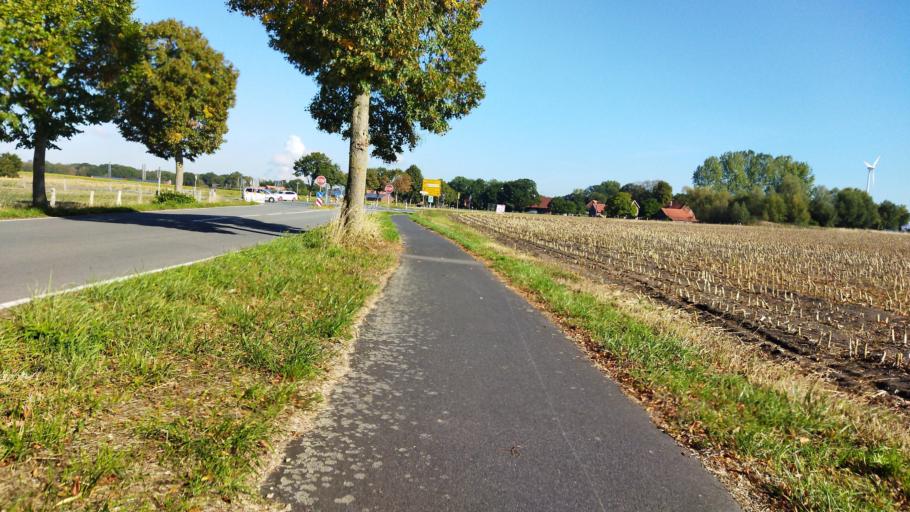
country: DE
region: Lower Saxony
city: Ohne
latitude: 52.2499
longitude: 7.3170
